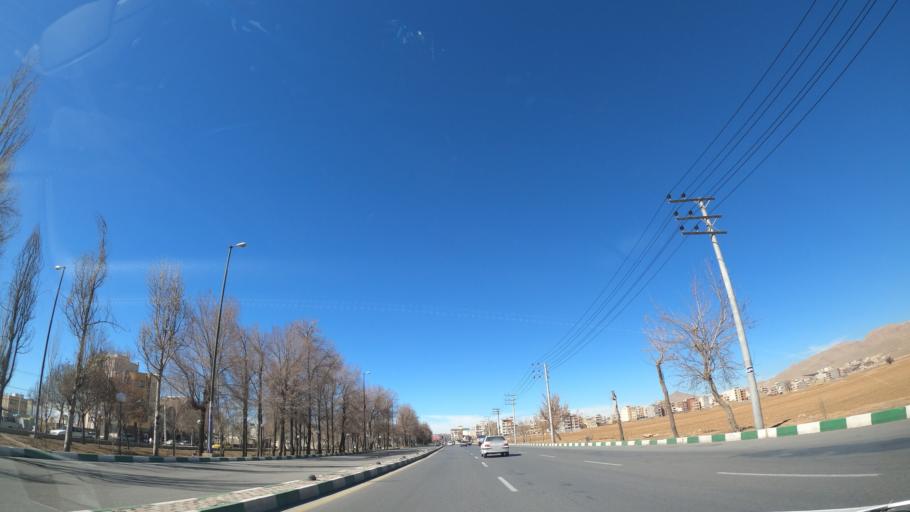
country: IR
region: Chahar Mahall va Bakhtiari
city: Shahrekord
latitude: 32.3096
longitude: 50.8939
